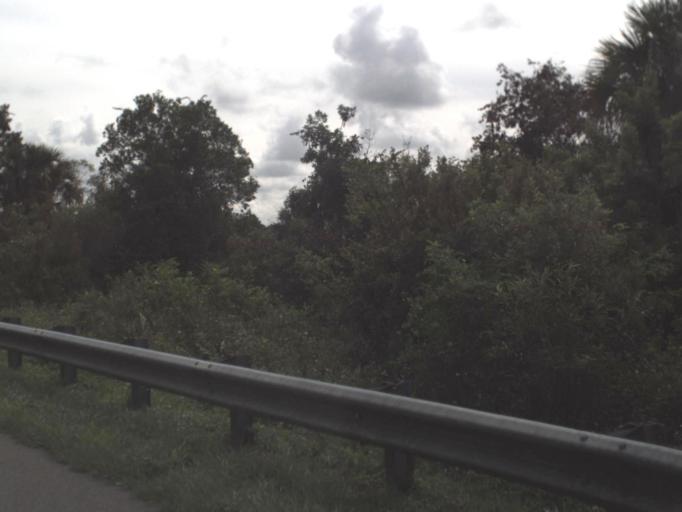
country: US
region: Florida
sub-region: Highlands County
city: Lake Placid
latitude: 27.2098
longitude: -81.1332
